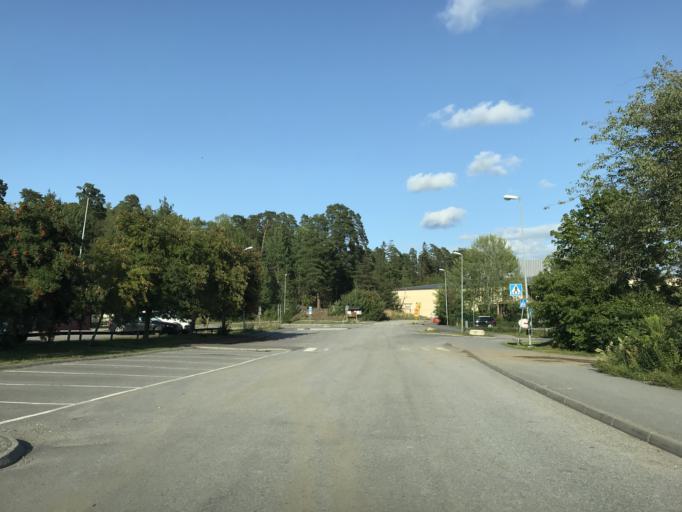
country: SE
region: Stockholm
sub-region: Sollentuna Kommun
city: Sollentuna
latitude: 59.4090
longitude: 17.9780
